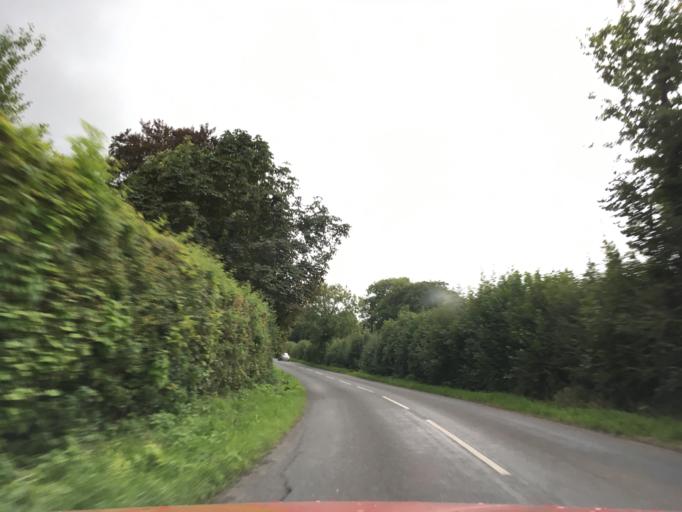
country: GB
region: Wales
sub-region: Monmouthshire
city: Llangybi
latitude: 51.6677
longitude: -2.8835
